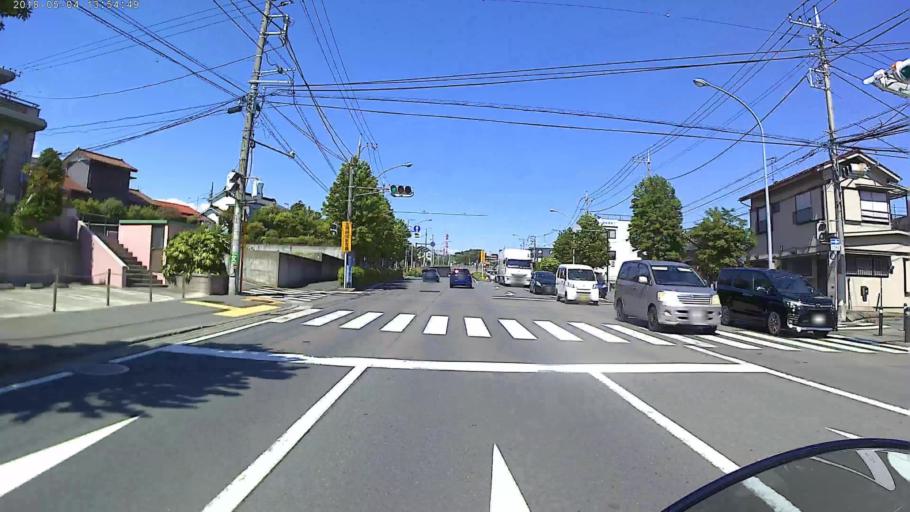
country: JP
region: Kanagawa
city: Minami-rinkan
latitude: 35.4689
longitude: 139.4942
